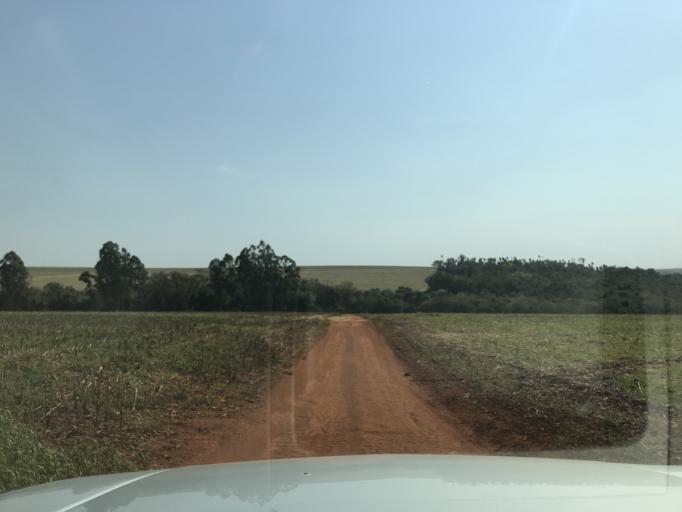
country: BR
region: Parana
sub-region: Palotina
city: Palotina
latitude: -24.2250
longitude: -53.7385
